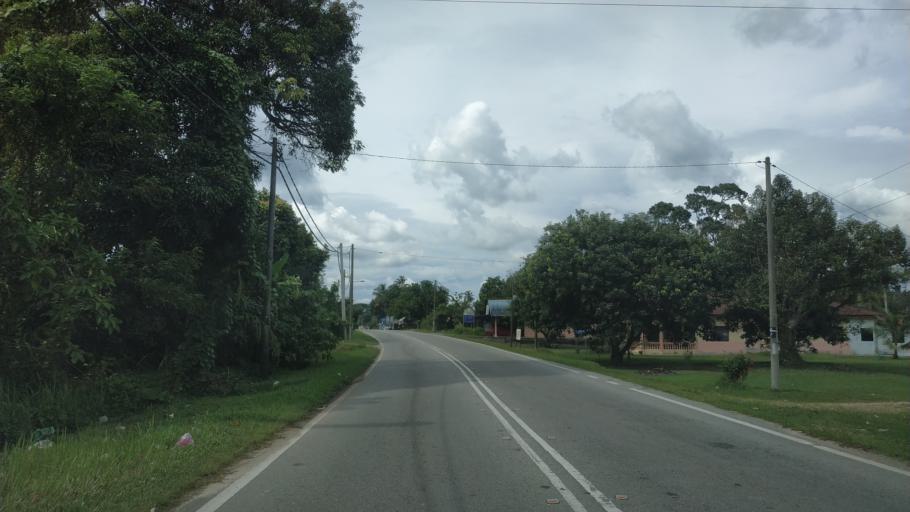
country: MY
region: Kedah
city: Kulim
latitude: 5.4227
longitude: 100.6652
